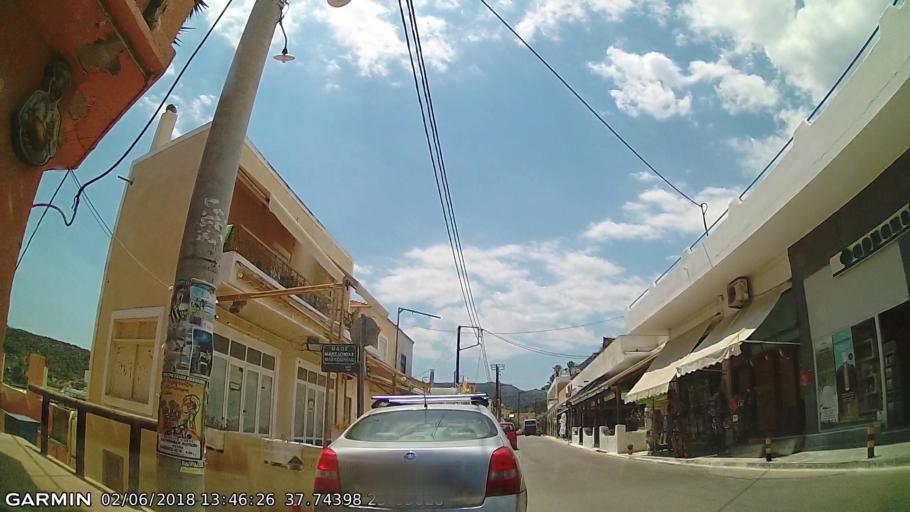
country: GR
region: Attica
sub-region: Nomos Piraios
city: Vathi
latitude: 37.7440
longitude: 23.5363
